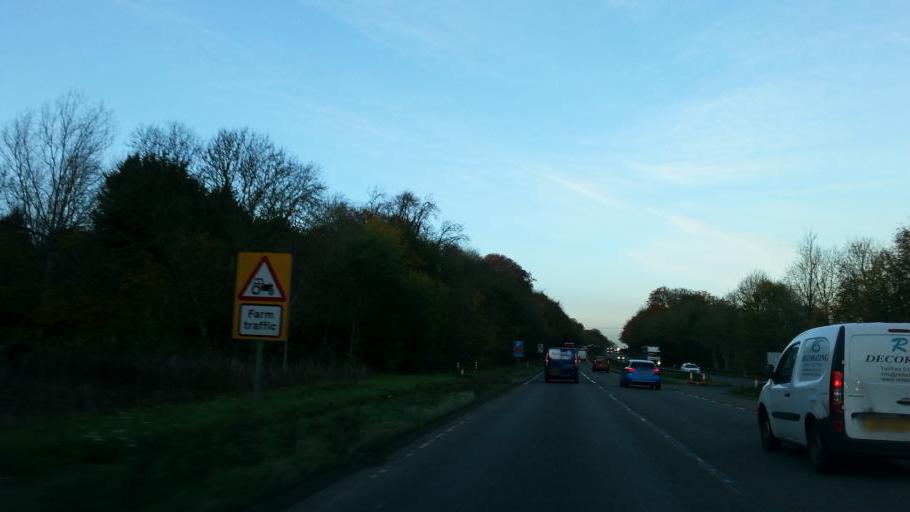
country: GB
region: England
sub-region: Lincolnshire
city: Grantham
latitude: 52.8399
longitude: -0.6290
